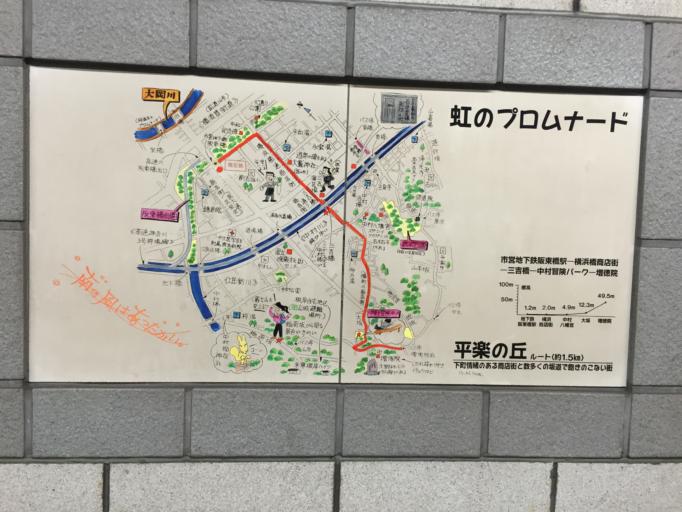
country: JP
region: Kanagawa
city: Yokohama
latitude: 35.4374
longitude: 139.6252
